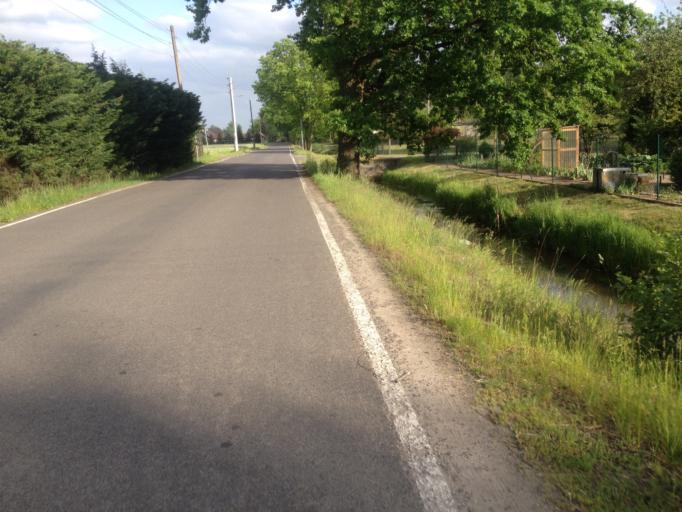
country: DE
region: Brandenburg
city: Cottbus
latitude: 51.8166
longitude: 14.3260
